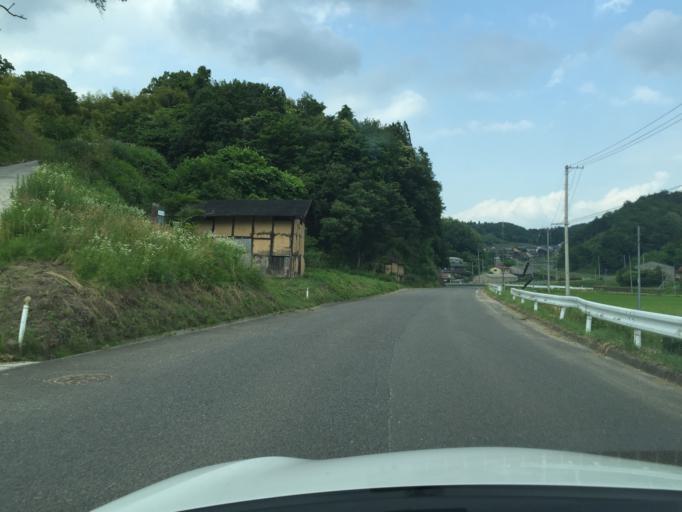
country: JP
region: Fukushima
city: Miharu
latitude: 37.3868
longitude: 140.4860
